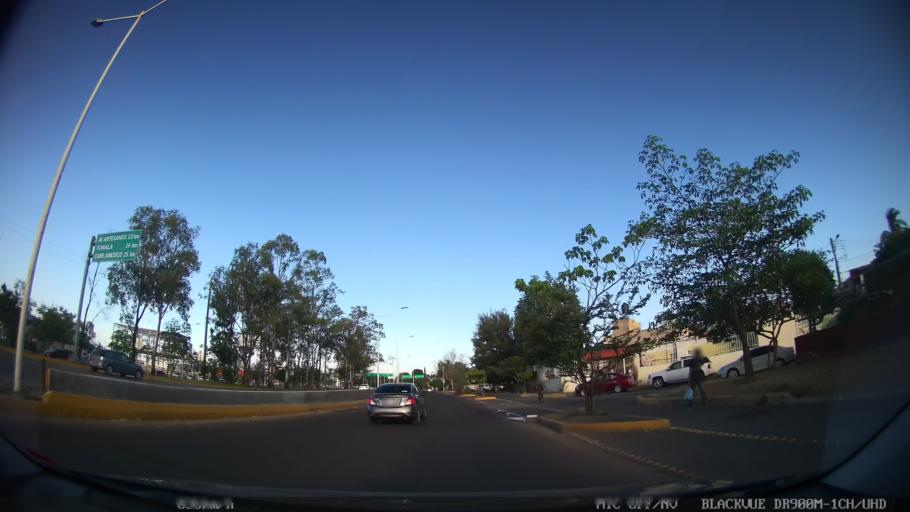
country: MX
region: Jalisco
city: Tlaquepaque
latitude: 20.7134
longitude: -103.3022
